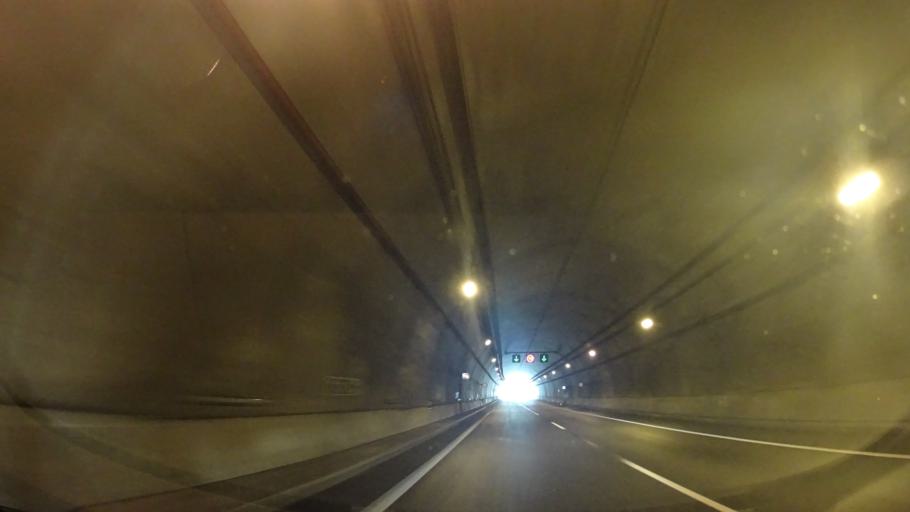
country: ES
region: Asturias
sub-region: Province of Asturias
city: Arriba
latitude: 43.4786
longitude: -5.5263
